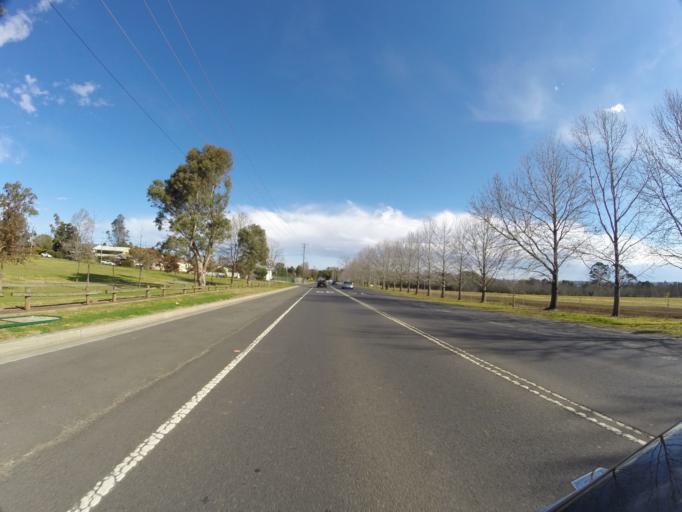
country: AU
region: New South Wales
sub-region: Camden
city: Elderslie
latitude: -34.0531
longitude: 150.7087
